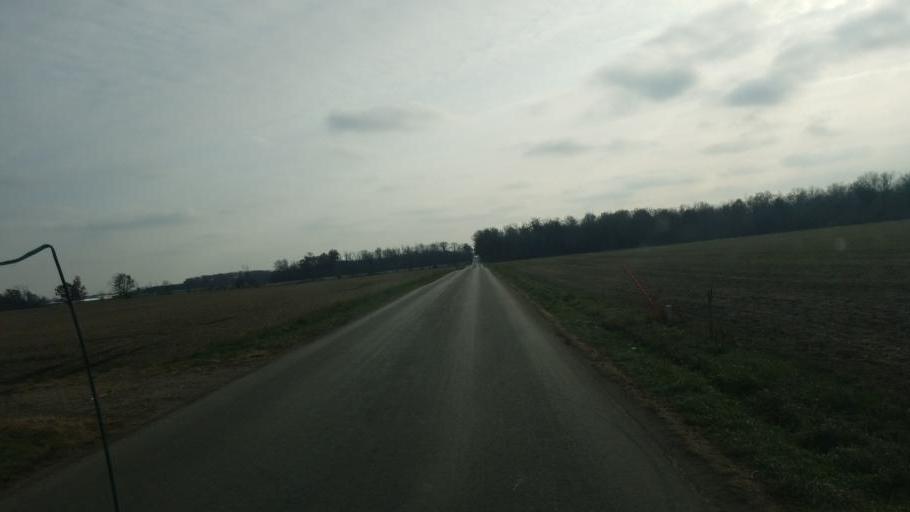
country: US
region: Indiana
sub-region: Adams County
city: Geneva
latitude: 40.6023
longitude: -84.9932
